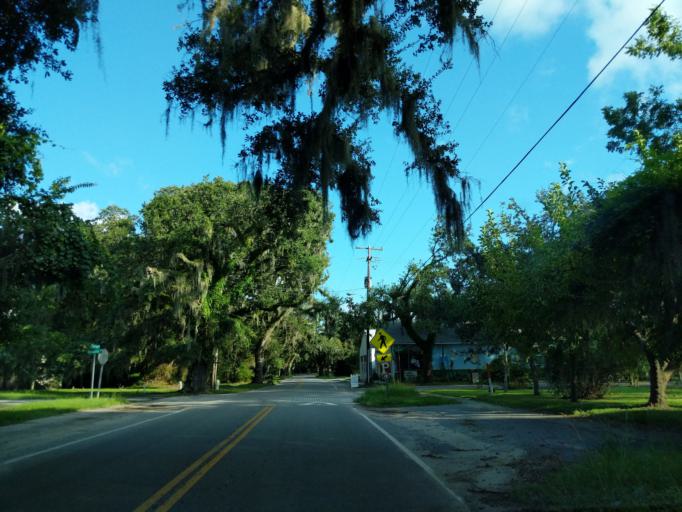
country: US
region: South Carolina
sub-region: Charleston County
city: Awendaw
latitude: 33.0897
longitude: -79.4624
